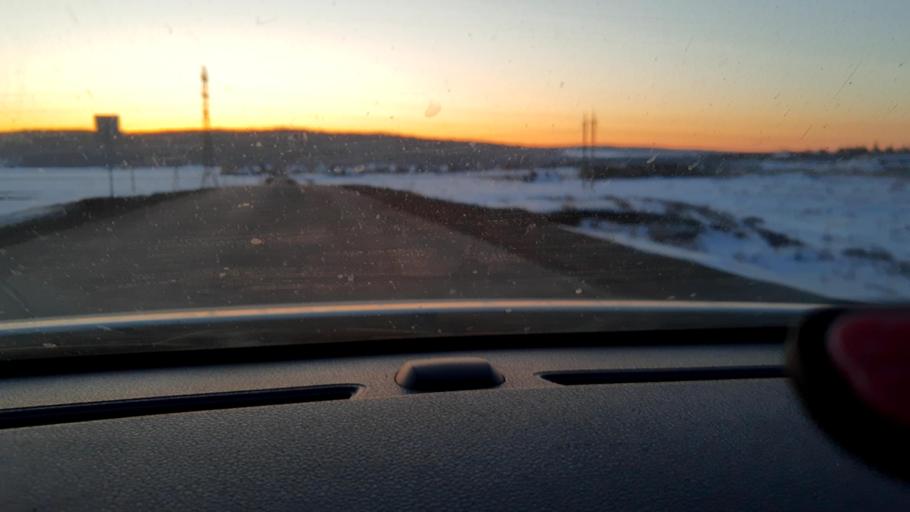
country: RU
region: Bashkortostan
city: Avdon
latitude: 54.3833
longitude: 55.7962
